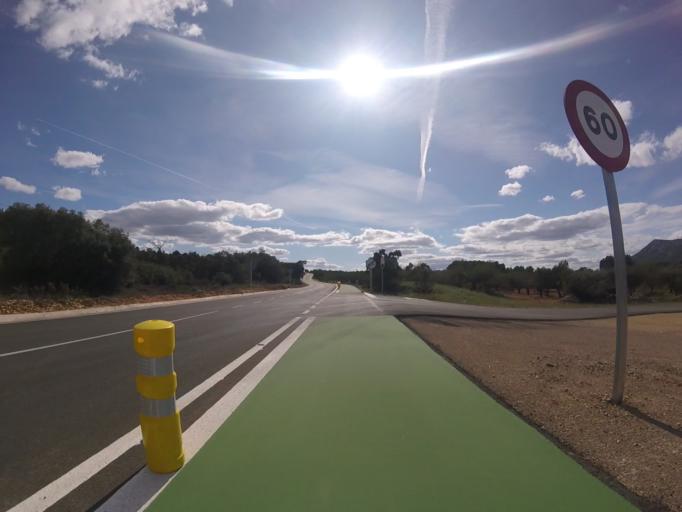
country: ES
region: Valencia
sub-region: Provincia de Castello
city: Cati
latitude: 40.4156
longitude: 0.0711
